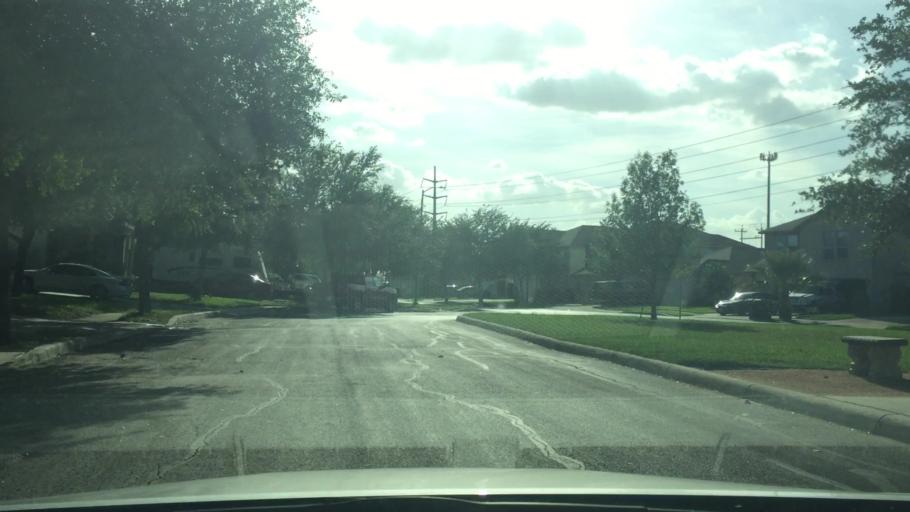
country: US
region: Texas
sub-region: Bexar County
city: Kirby
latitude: 29.4628
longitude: -98.3569
